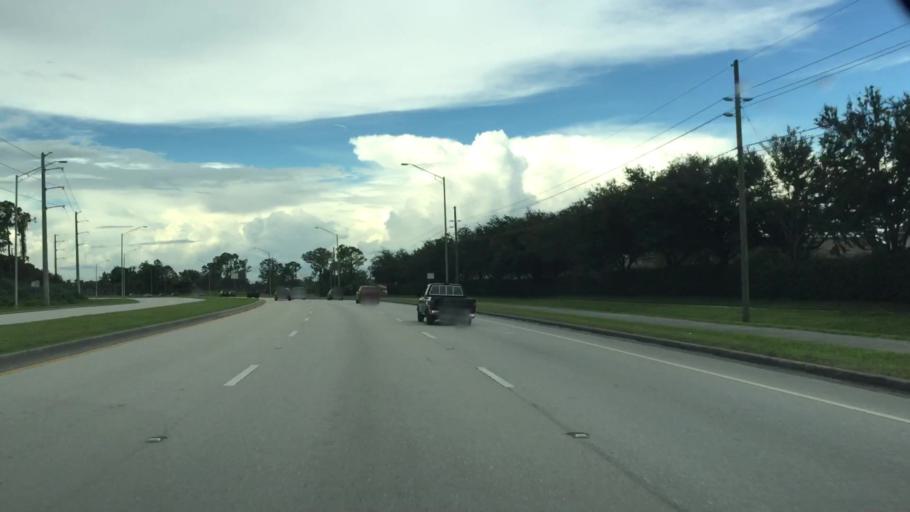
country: US
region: Florida
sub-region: Collier County
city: Orangetree
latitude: 26.2810
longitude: -81.5959
